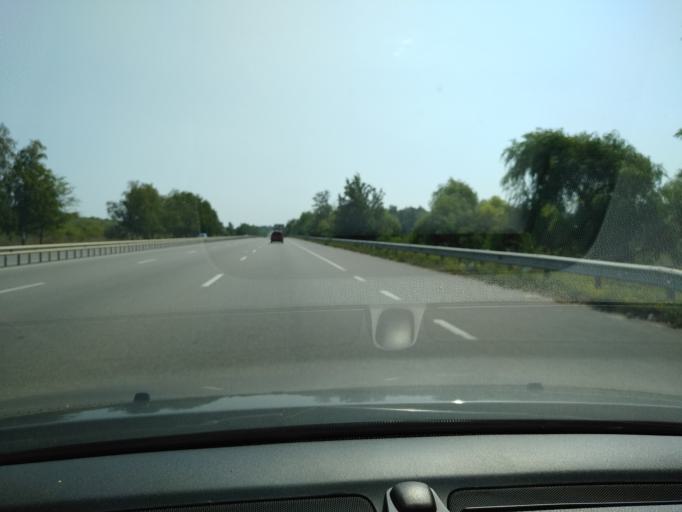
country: MD
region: Chisinau
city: Cricova
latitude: 47.1293
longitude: 28.8458
